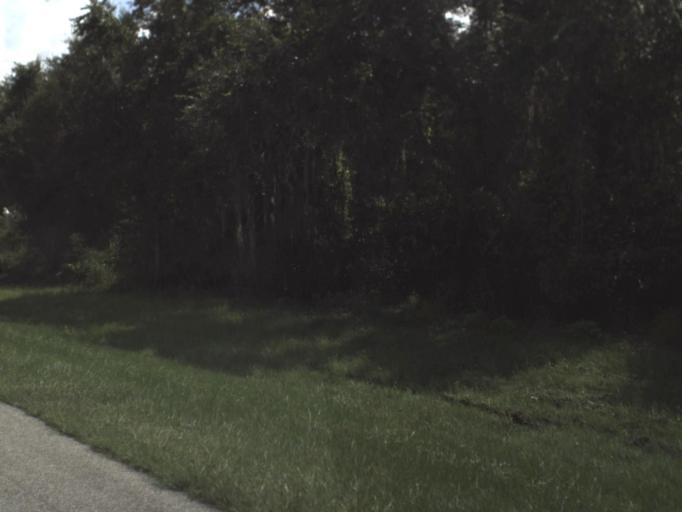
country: US
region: Florida
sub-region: Sarasota County
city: Lake Sarasota
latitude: 27.2410
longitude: -82.3188
